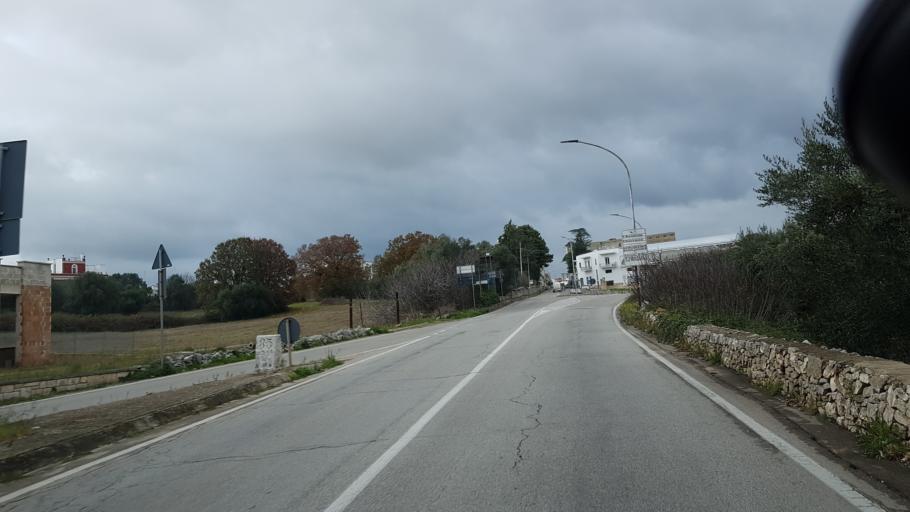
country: IT
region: Apulia
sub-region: Provincia di Bari
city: Alberobello
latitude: 40.7822
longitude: 17.2441
